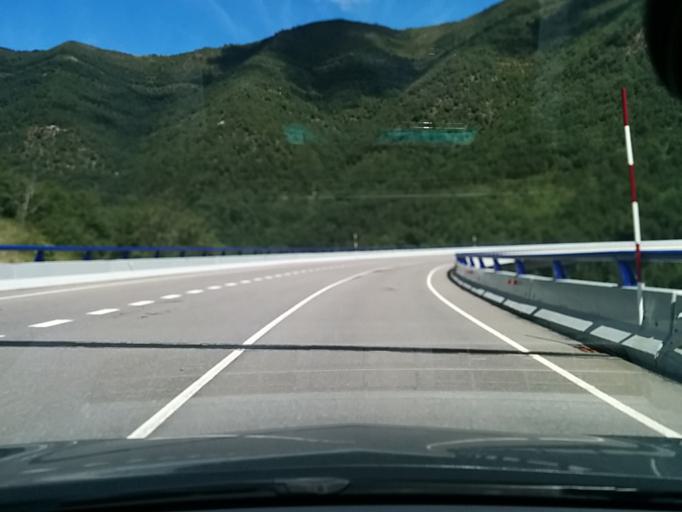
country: ES
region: Aragon
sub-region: Provincia de Huesca
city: Fiscal
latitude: 42.4978
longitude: -0.1534
